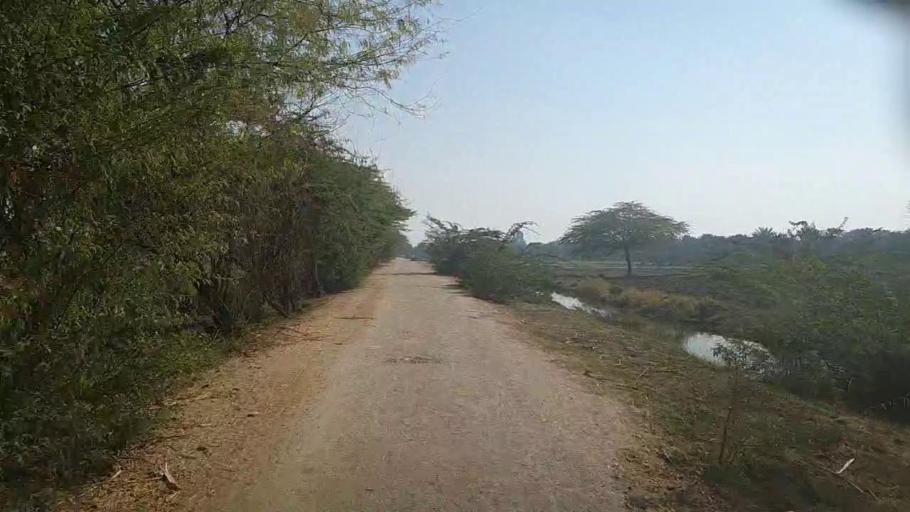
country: PK
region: Sindh
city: Kot Diji
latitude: 27.4366
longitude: 68.7135
